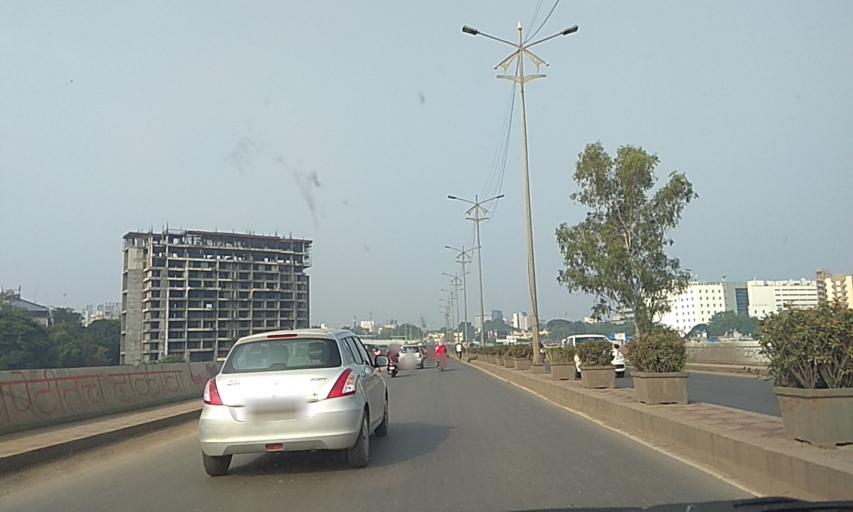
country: IN
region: Maharashtra
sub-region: Pune Division
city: Shivaji Nagar
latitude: 18.5328
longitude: 73.8569
